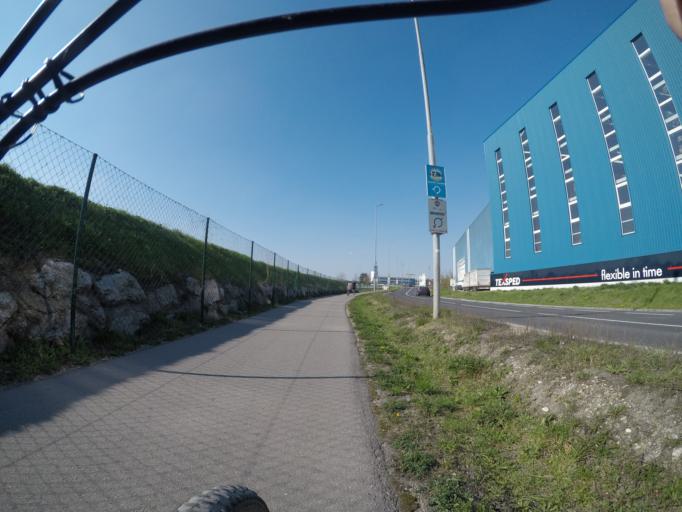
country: AT
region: Lower Austria
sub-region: Politischer Bezirk Modling
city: Neu-Guntramsdorf
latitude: 48.0608
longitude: 16.3358
